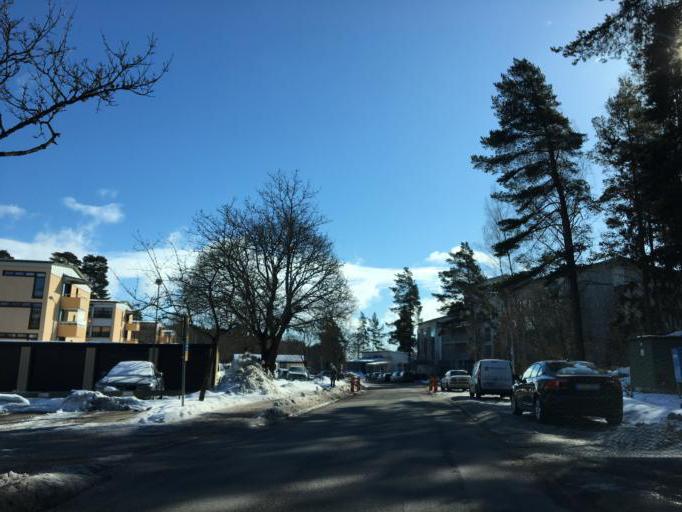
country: SE
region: Vaestmanland
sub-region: Vasteras
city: Vasteras
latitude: 59.6107
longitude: 16.5074
